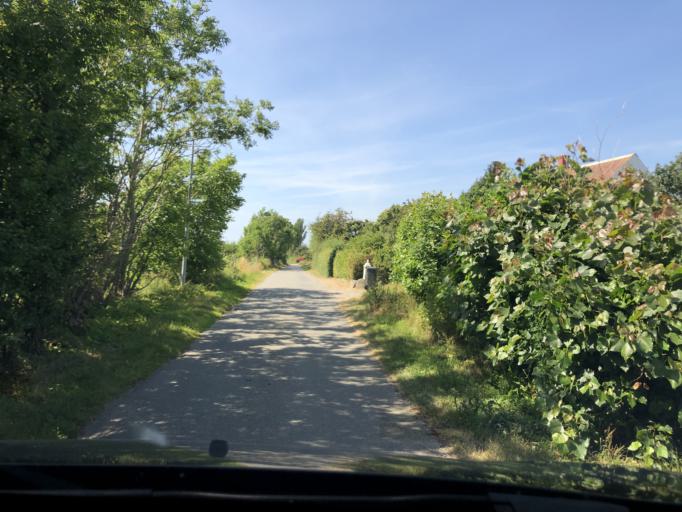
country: DK
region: South Denmark
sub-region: AEro Kommune
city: AEroskobing
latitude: 54.9006
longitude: 10.2815
